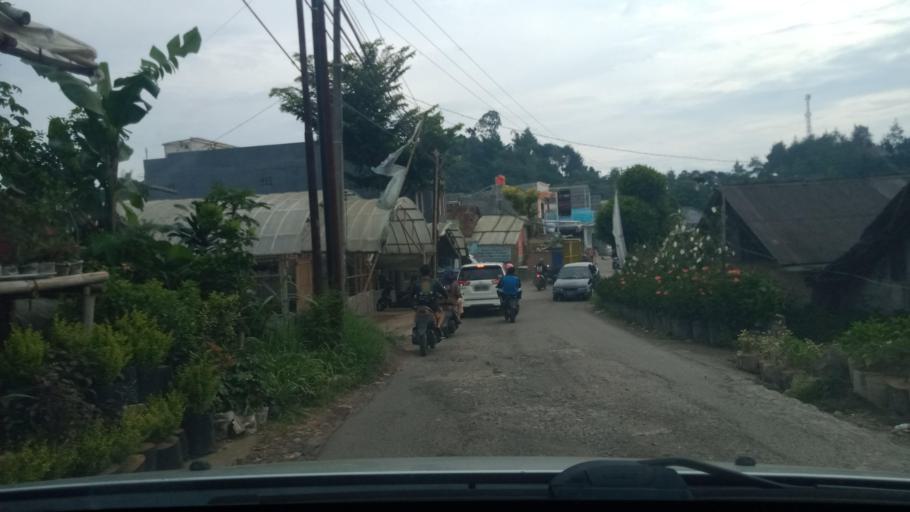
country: ID
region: West Java
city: Lembang
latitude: -6.8159
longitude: 107.5883
